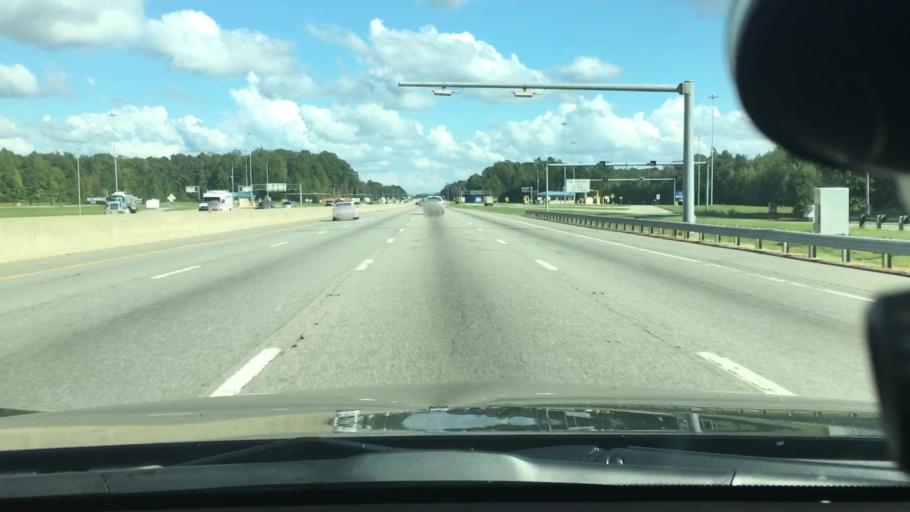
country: US
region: North Carolina
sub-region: Alamance County
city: Mebane
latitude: 36.0778
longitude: -79.2112
